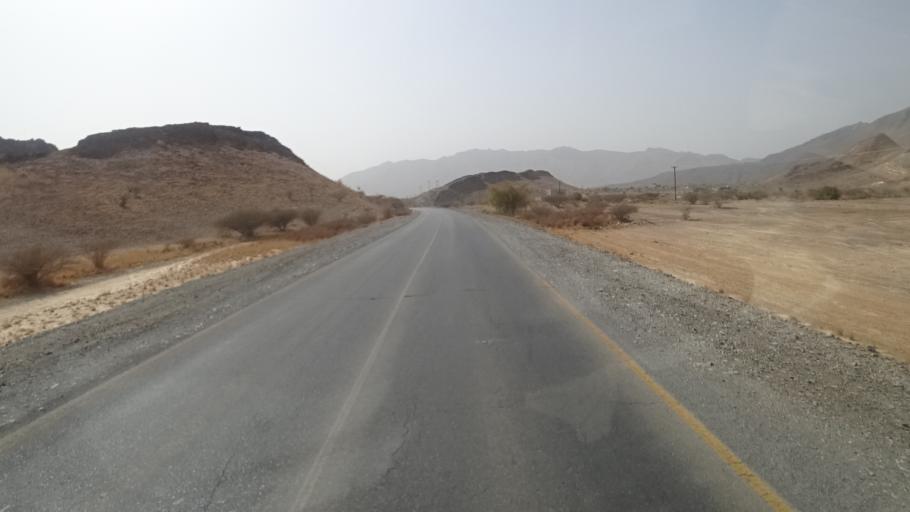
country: OM
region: Muhafazat ad Dakhiliyah
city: Nizwa
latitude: 22.9259
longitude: 57.6313
